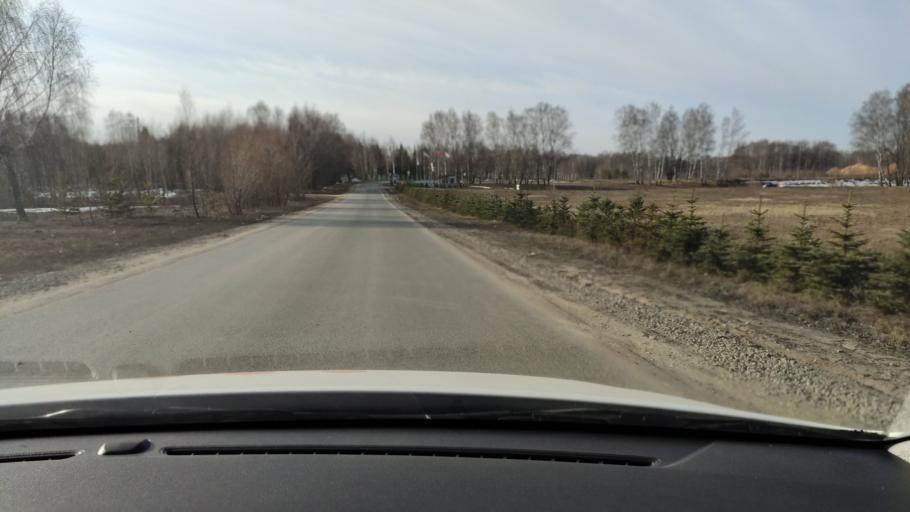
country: RU
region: Tatarstan
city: Osinovo
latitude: 55.8458
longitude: 48.9167
